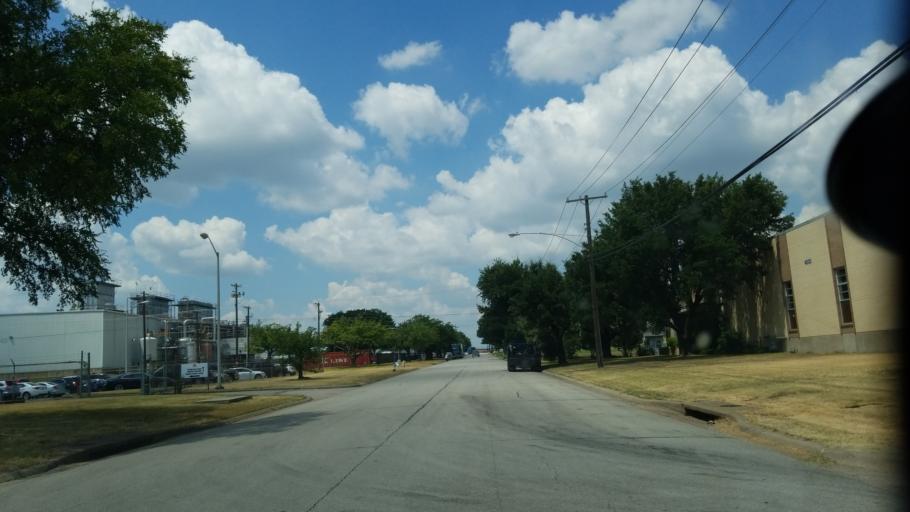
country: US
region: Texas
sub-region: Dallas County
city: Duncanville
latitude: 32.6852
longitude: -96.8853
